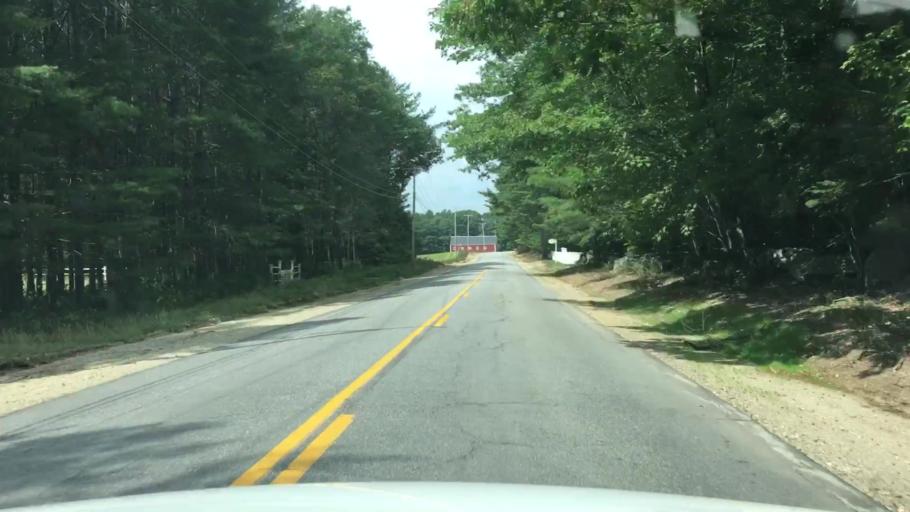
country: US
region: Maine
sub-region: Oxford County
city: Rumford
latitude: 44.5324
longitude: -70.6667
